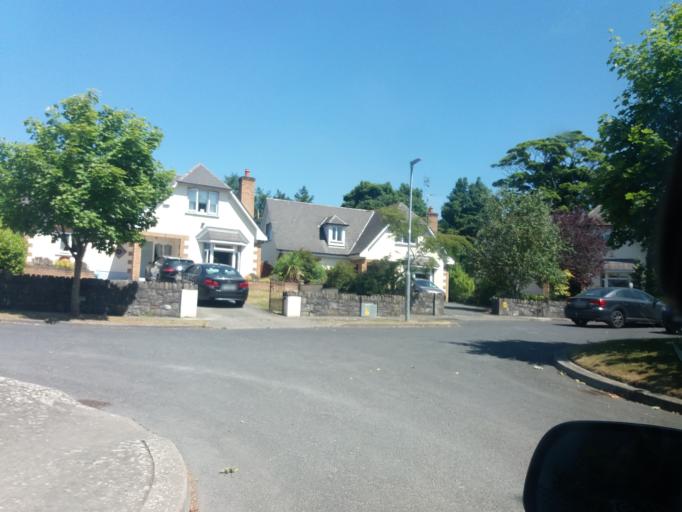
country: IE
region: Leinster
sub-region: Fingal County
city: Swords
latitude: 53.5203
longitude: -6.2663
